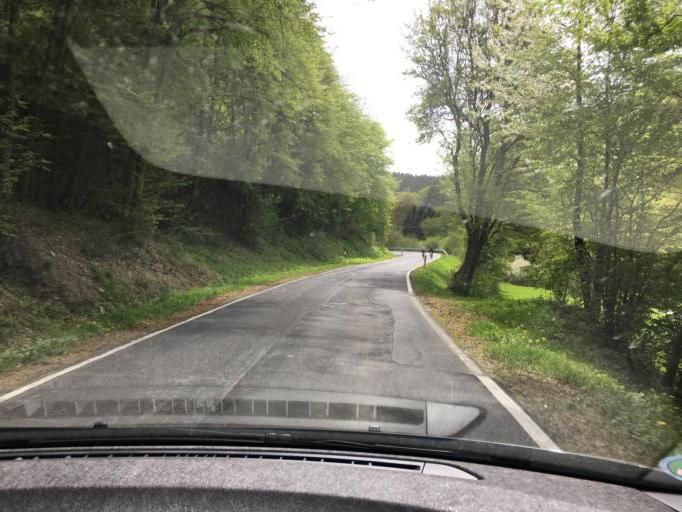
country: DE
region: Rheinland-Pfalz
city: Heckenbach
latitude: 50.4686
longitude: 7.0622
